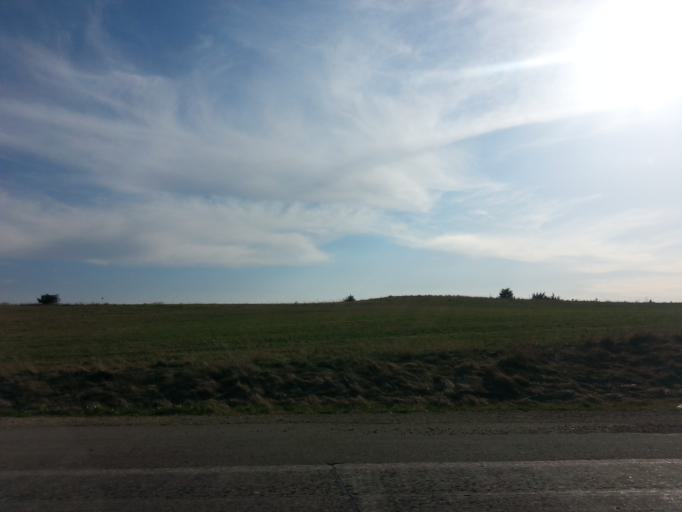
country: US
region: Wisconsin
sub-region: Pierce County
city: River Falls
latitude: 44.7425
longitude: -92.6402
